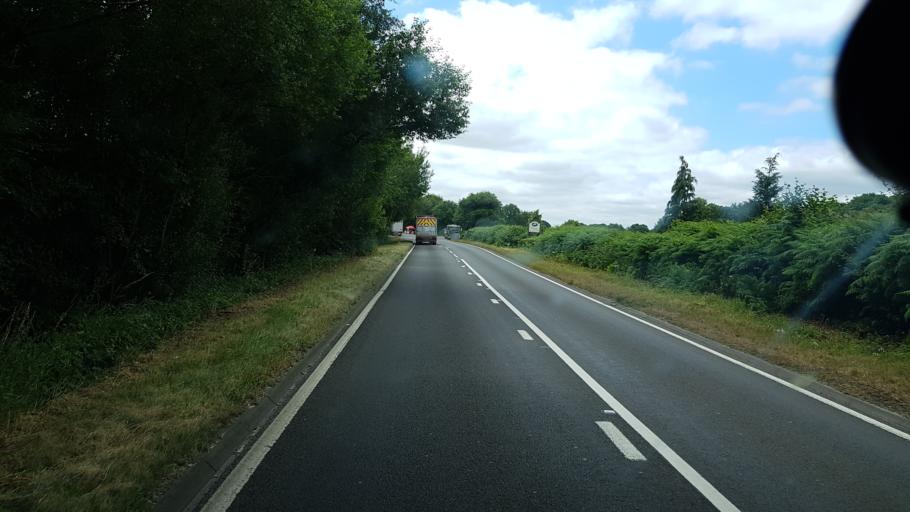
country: GB
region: England
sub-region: Surrey
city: Lingfield
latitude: 51.1775
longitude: -0.0475
